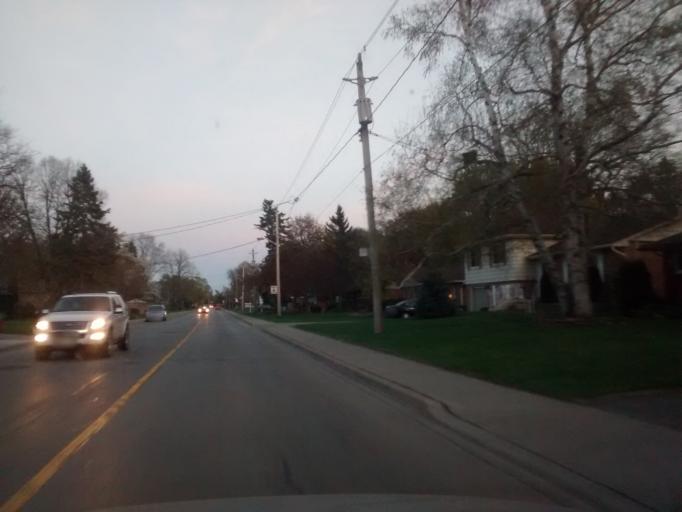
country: CA
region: Ontario
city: Burlington
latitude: 43.3399
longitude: -79.8000
